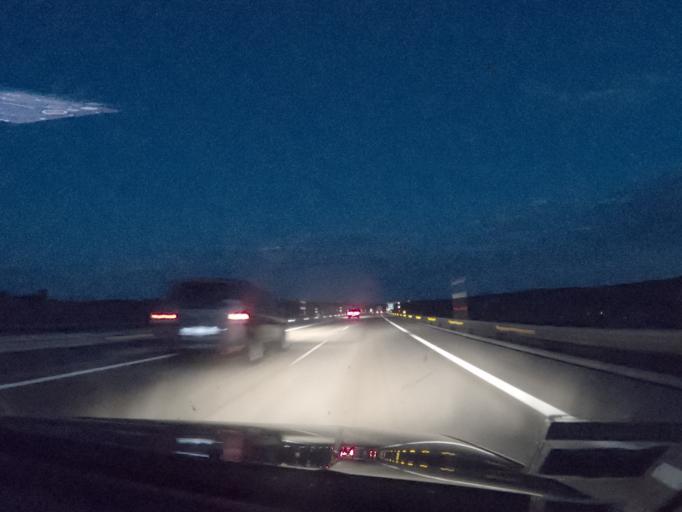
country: ES
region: Castille and Leon
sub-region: Provincia de Leon
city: Brazuelo
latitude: 42.5585
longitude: -6.1913
